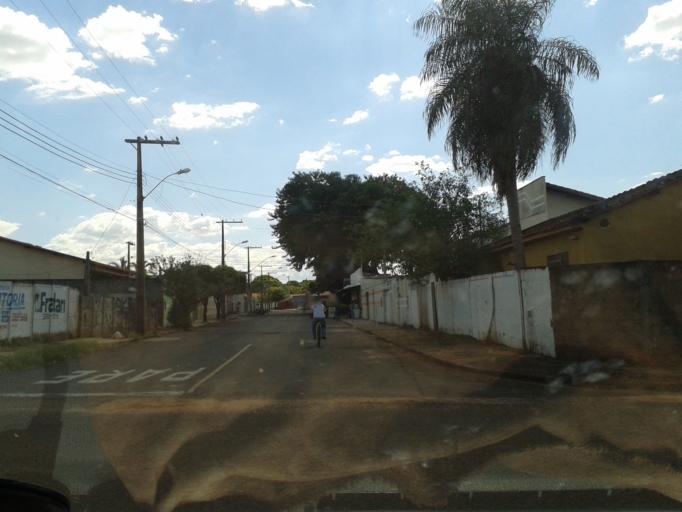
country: BR
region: Minas Gerais
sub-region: Ituiutaba
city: Ituiutaba
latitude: -18.9848
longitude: -49.4499
